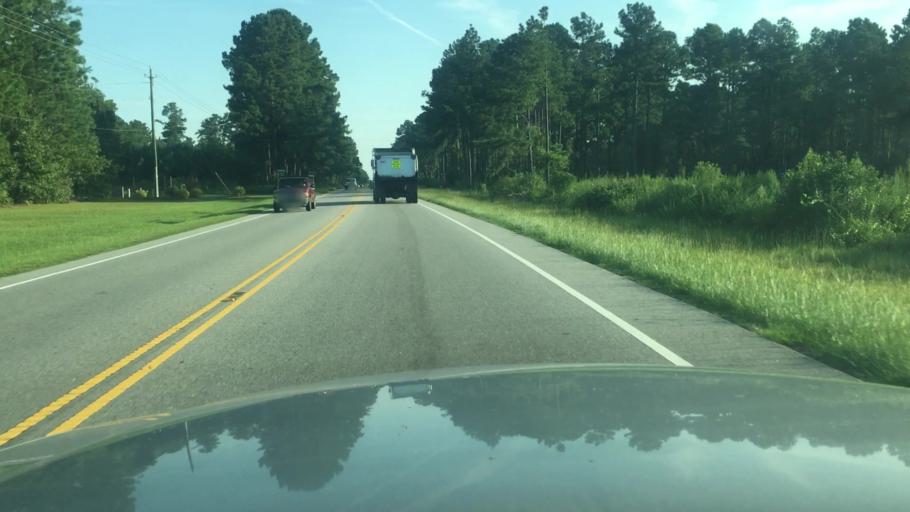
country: US
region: North Carolina
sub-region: Harnett County
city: Walkertown
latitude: 35.1949
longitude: -78.8495
